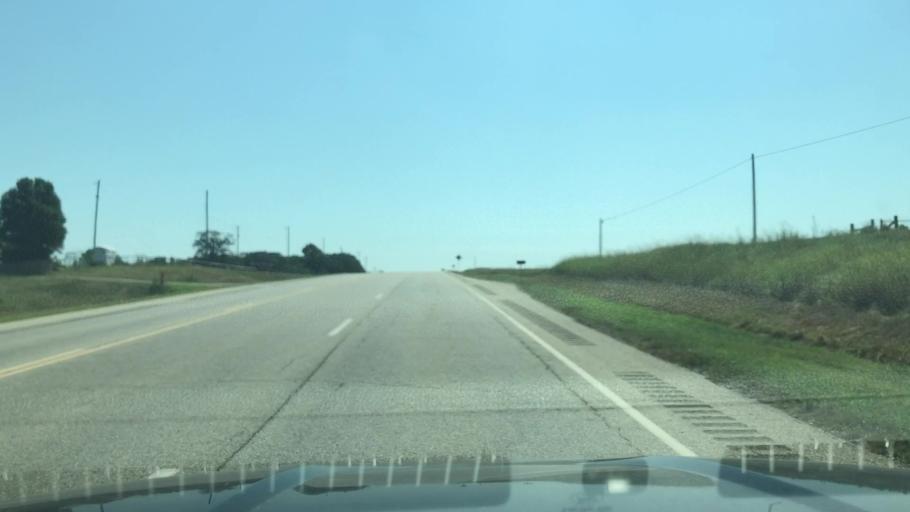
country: US
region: Oklahoma
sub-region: Creek County
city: Mannford
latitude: 36.0030
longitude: -96.4183
